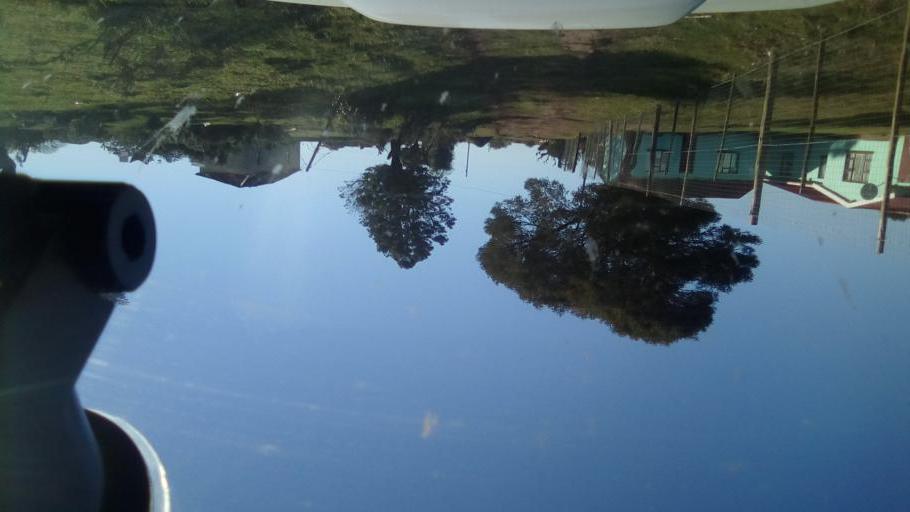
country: ZA
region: Eastern Cape
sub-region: Buffalo City Metropolitan Municipality
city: Bhisho
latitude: -32.9486
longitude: 27.2955
